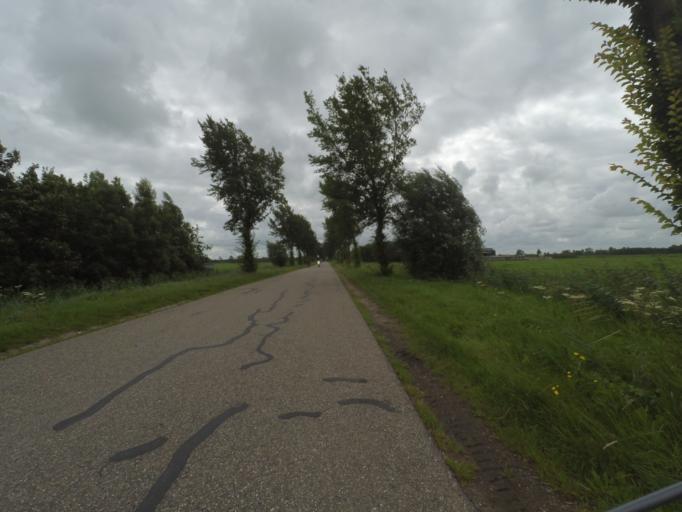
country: NL
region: Friesland
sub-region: Gemeente Kollumerland en Nieuwkruisland
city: Kollumerzwaag
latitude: 53.3035
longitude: 6.0883
